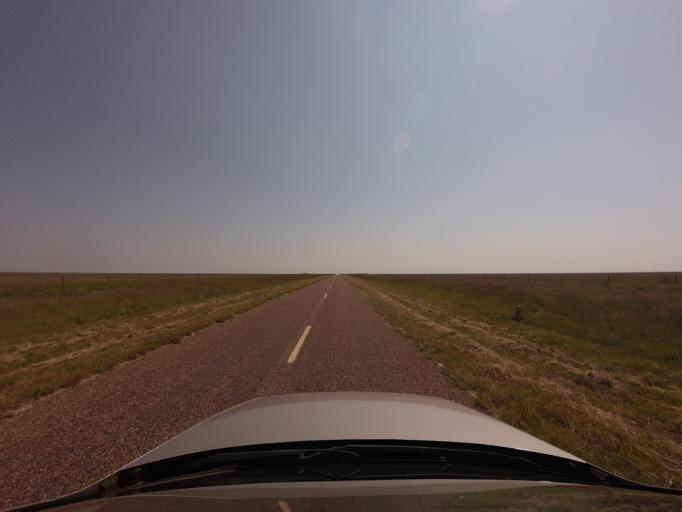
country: US
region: New Mexico
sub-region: Curry County
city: Cannon Air Force Base
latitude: 34.6333
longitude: -103.4451
